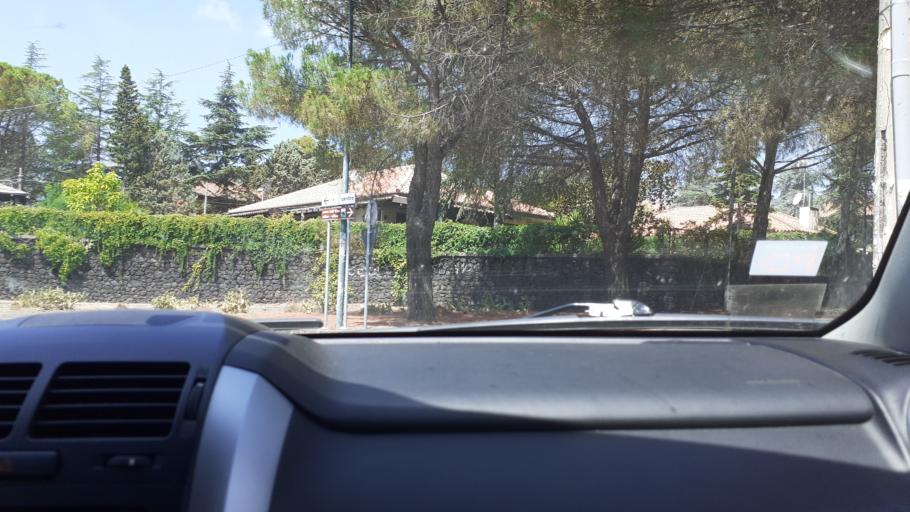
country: IT
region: Sicily
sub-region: Catania
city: Nicolosi
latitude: 37.6207
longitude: 15.0279
